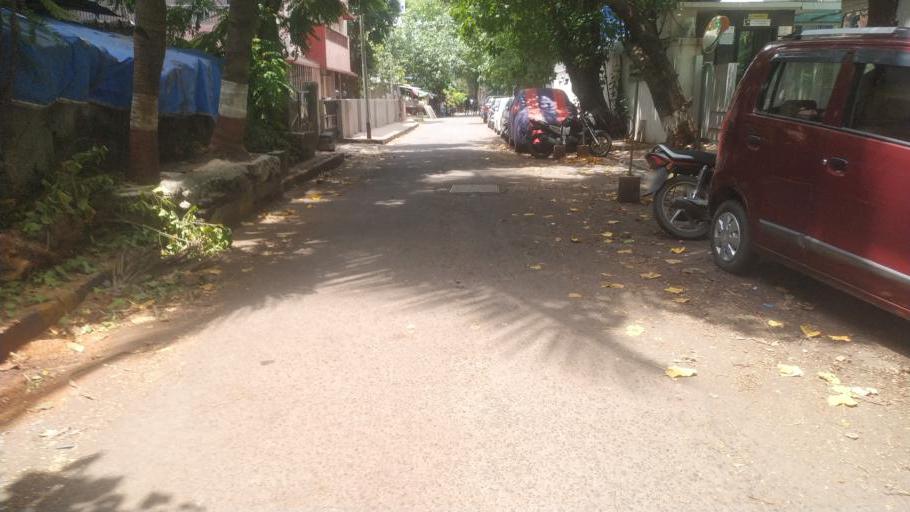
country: IN
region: Maharashtra
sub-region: Mumbai Suburban
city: Mumbai
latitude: 19.0190
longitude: 72.8347
